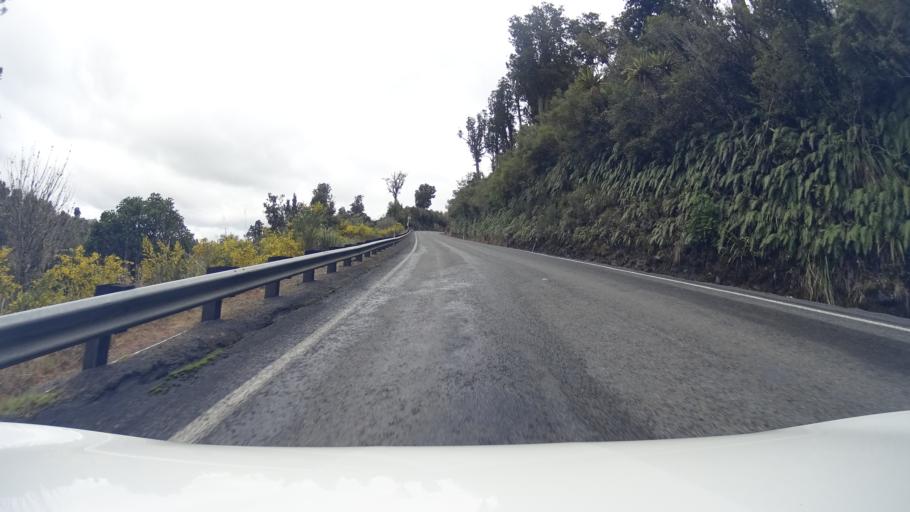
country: NZ
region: Manawatu-Wanganui
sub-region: Ruapehu District
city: Waiouru
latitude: -39.2637
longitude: 175.3944
